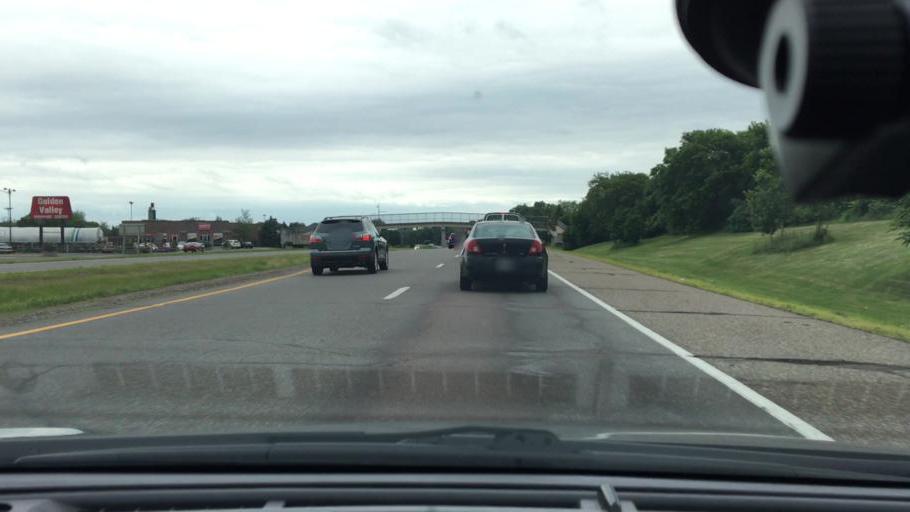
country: US
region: Minnesota
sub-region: Hennepin County
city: Golden Valley
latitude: 44.9843
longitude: -93.3838
